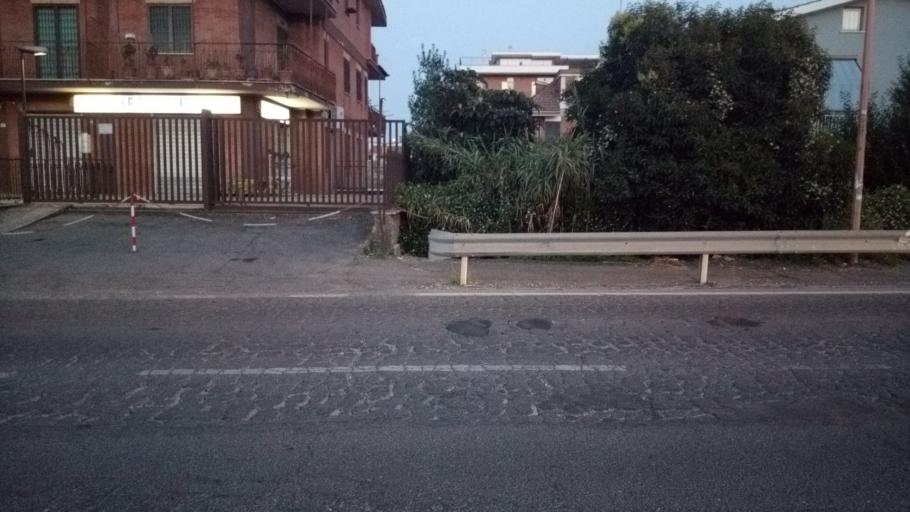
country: IT
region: Latium
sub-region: Citta metropolitana di Roma Capitale
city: Ciampino
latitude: 41.8102
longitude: 12.6012
